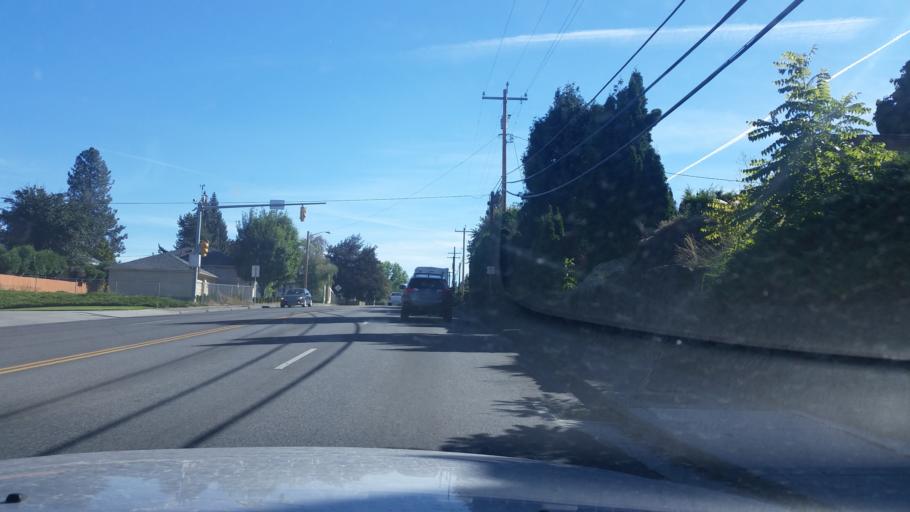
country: US
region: Washington
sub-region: Spokane County
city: Spokane
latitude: 47.6391
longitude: -117.3632
